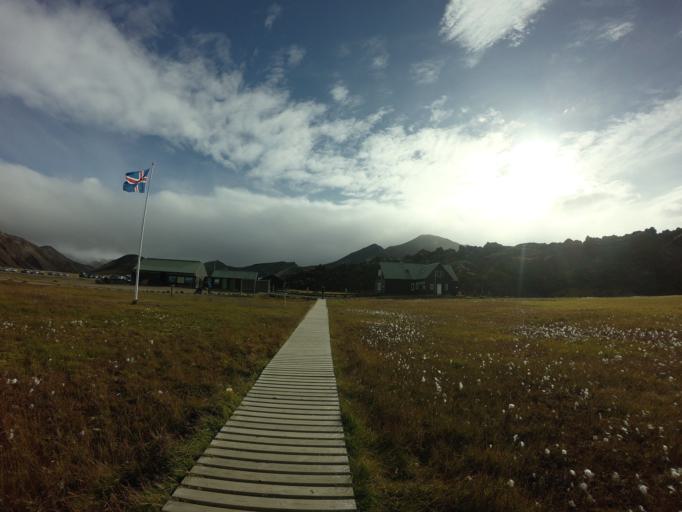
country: IS
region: South
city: Vestmannaeyjar
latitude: 63.9911
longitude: -19.0610
